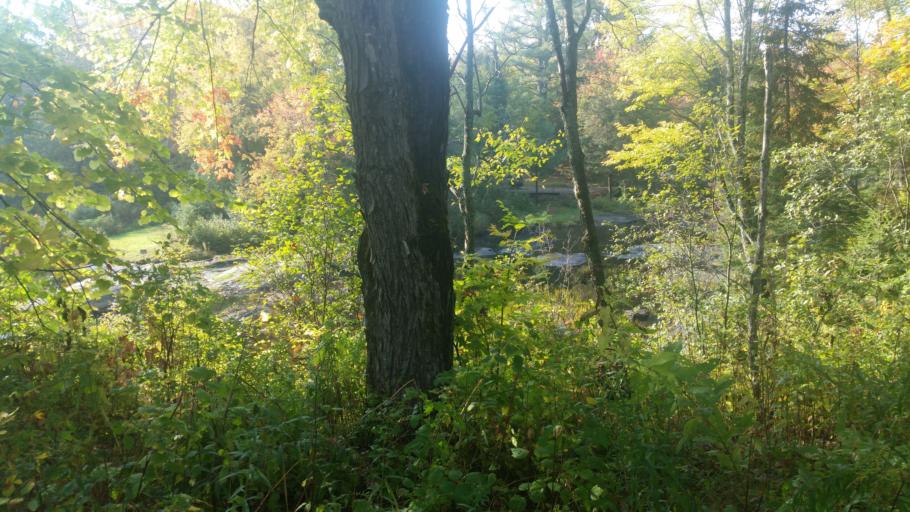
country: CA
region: Ontario
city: Bracebridge
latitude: 45.2397
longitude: -79.5829
